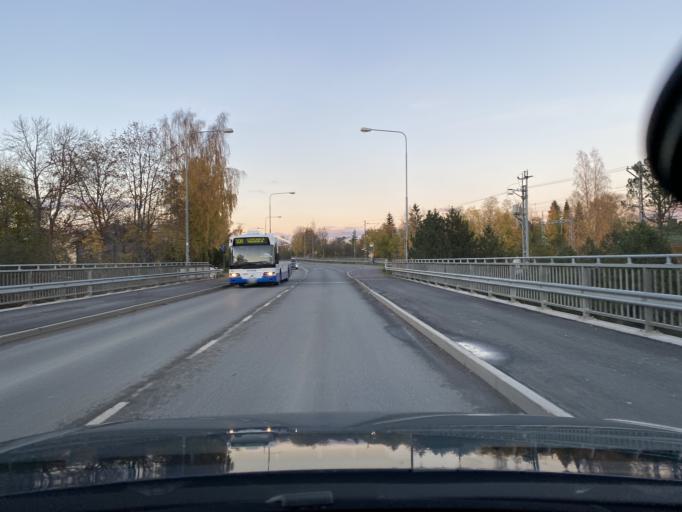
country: FI
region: Pirkanmaa
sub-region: Tampere
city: Lempaeaelae
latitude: 61.3071
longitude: 23.7516
